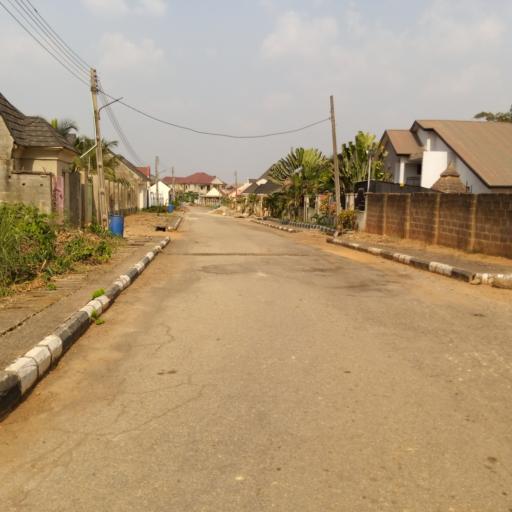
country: NG
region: Oyo
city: Ibadan
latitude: 7.4282
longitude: 3.9089
